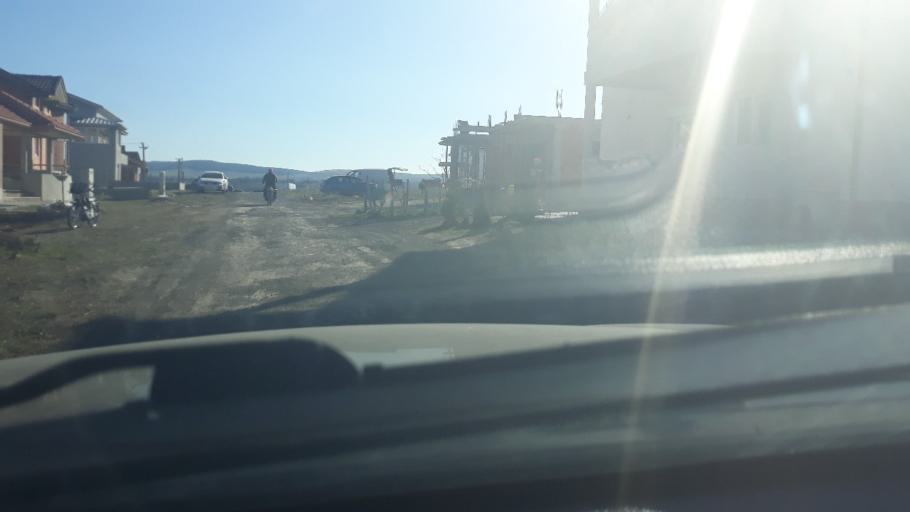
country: MK
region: Sveti Nikole
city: Sveti Nikole
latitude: 41.8695
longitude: 21.9303
